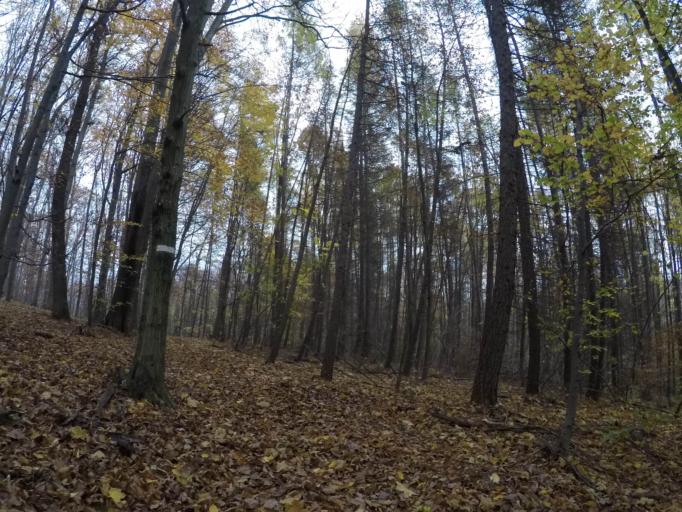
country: SK
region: Presovsky
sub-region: Okres Presov
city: Presov
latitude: 48.9680
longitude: 21.1886
